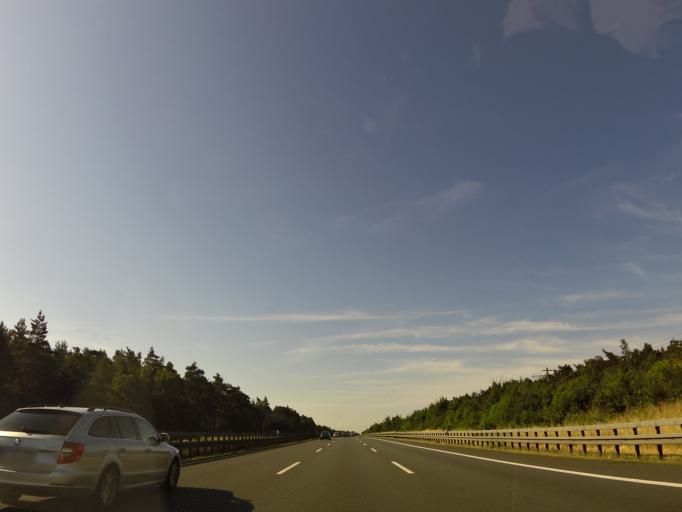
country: DE
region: Bavaria
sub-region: Regierungsbezirk Mittelfranken
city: Schwarzenbruck
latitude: 49.3203
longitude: 11.2065
